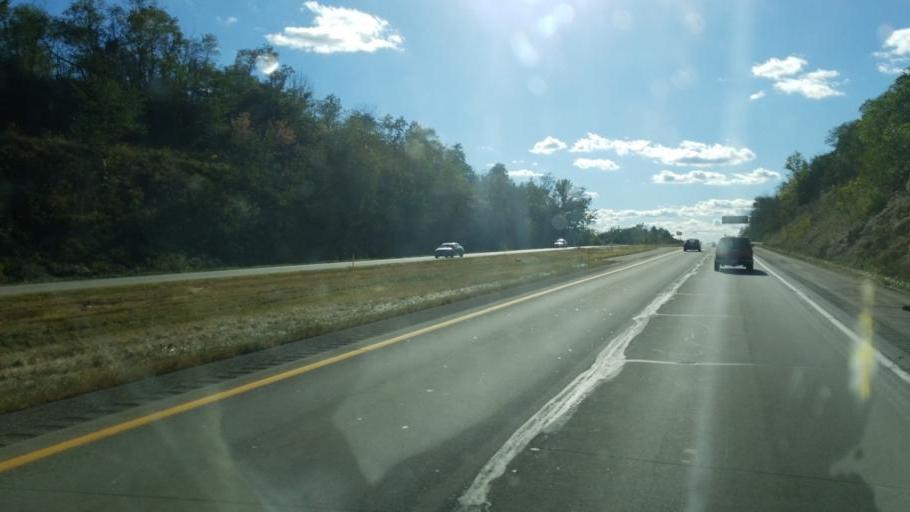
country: US
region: West Virginia
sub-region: Ohio County
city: West Liberty
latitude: 40.0964
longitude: -80.5170
